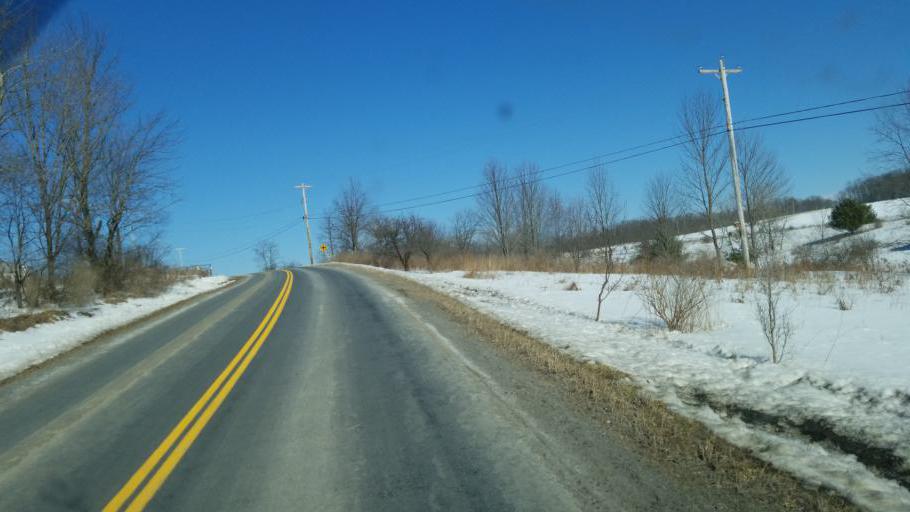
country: US
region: New York
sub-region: Allegany County
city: Andover
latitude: 42.0987
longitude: -77.7049
